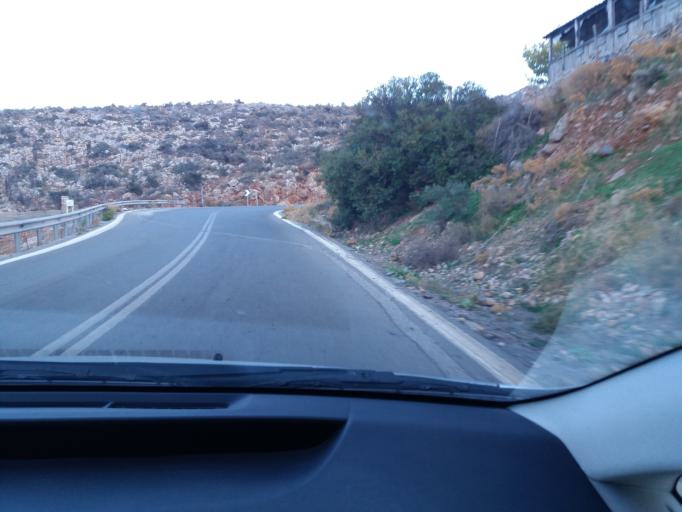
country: GR
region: Crete
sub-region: Nomos Irakleiou
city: Mokhos
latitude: 35.2751
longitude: 25.4287
